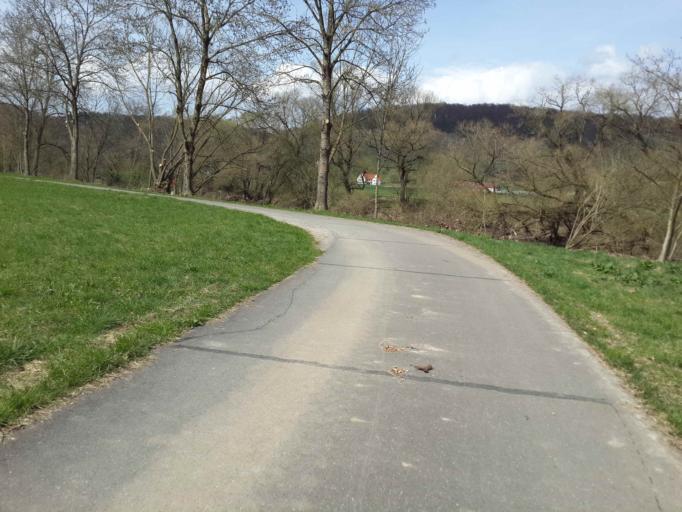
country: DE
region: Baden-Wuerttemberg
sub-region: Regierungsbezirk Stuttgart
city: Krautheim
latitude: 49.3878
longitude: 9.6601
